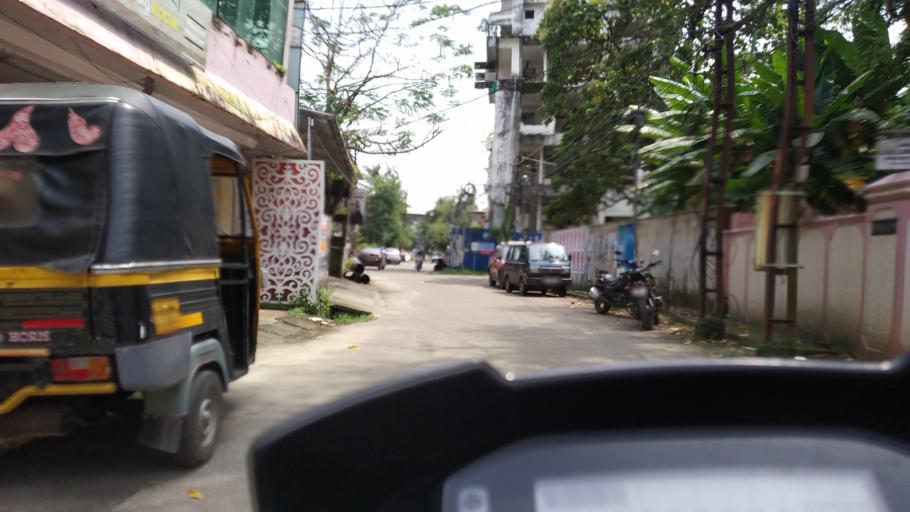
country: IN
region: Kerala
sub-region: Ernakulam
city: Cochin
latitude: 9.9604
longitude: 76.2915
